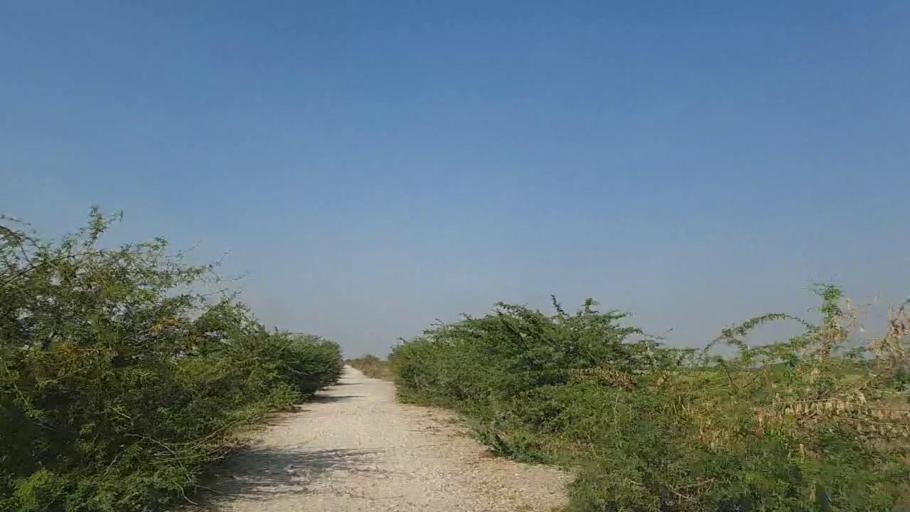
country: PK
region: Sindh
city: Naukot
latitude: 24.9159
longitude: 69.4878
